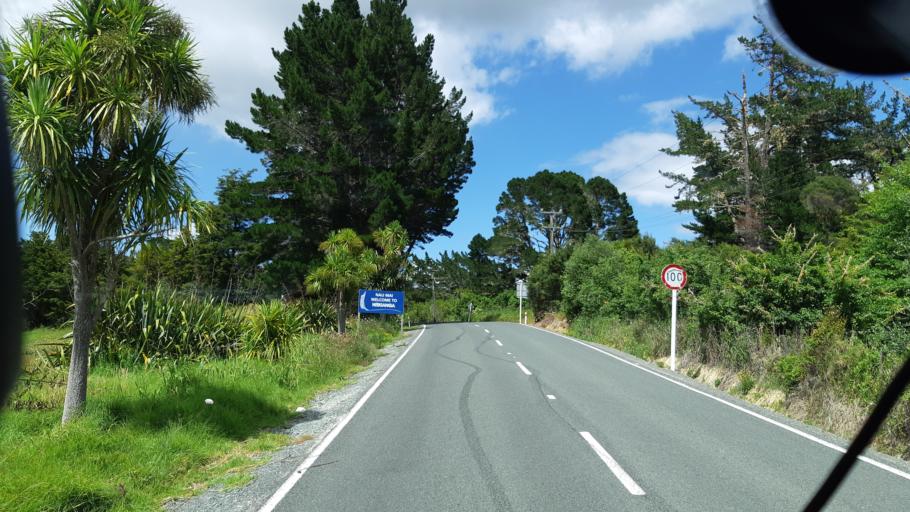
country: NZ
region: Northland
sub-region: Far North District
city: Taipa
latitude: -35.2375
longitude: 173.5430
